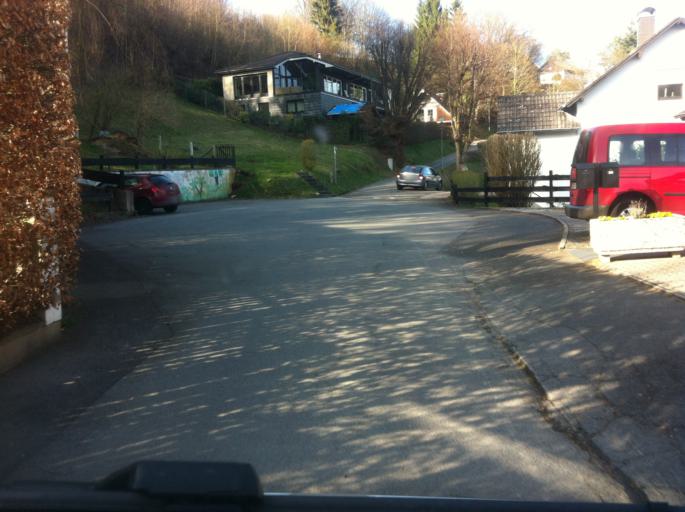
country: DE
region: North Rhine-Westphalia
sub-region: Regierungsbezirk Koln
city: Simmerath
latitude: 50.6125
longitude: 6.3757
